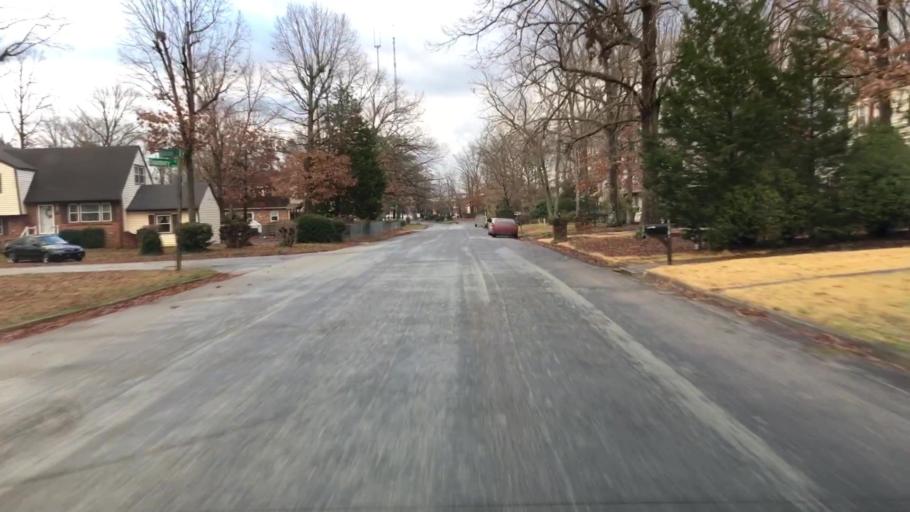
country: US
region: Virginia
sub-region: Chesterfield County
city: Bon Air
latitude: 37.5120
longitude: -77.6176
